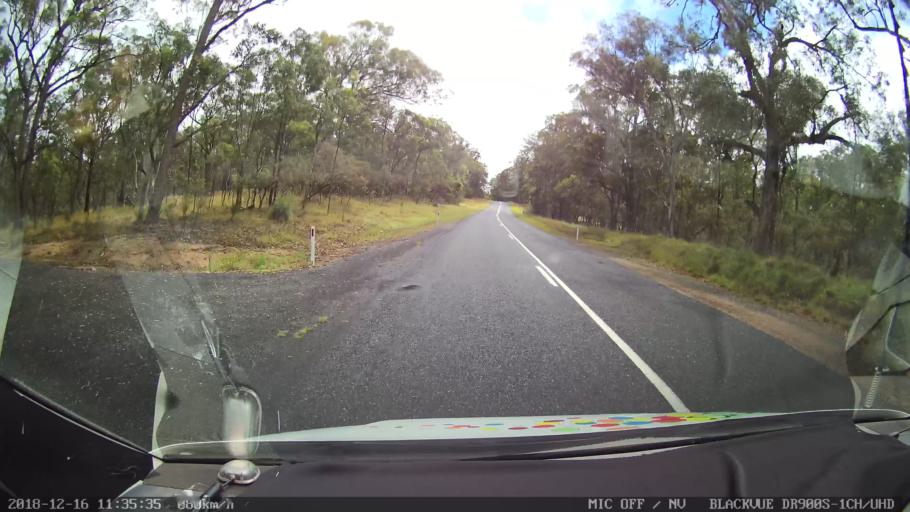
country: AU
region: New South Wales
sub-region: Tenterfield Municipality
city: Carrolls Creek
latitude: -28.9884
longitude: 152.1637
